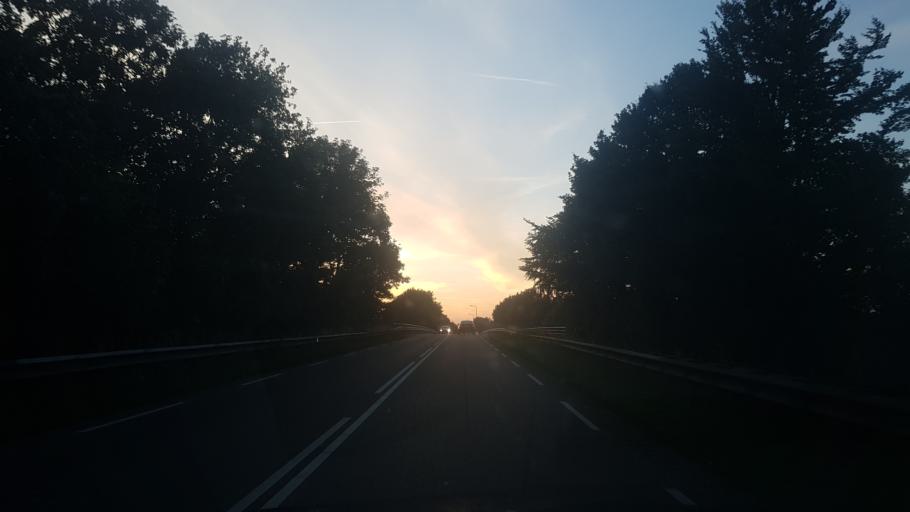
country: NL
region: Flevoland
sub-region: Gemeente Noordoostpolder
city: Emmeloord
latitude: 52.6954
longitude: 5.7280
